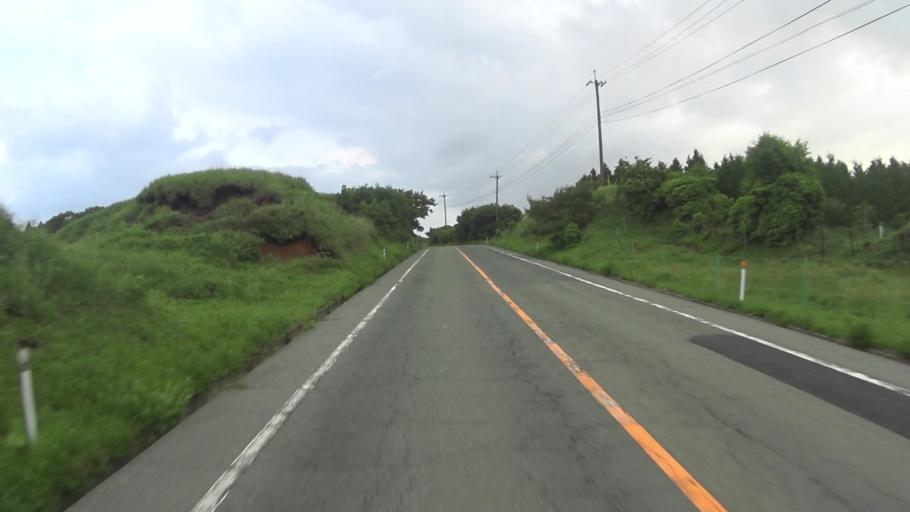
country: JP
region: Kumamoto
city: Aso
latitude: 32.9545
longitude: 130.9861
